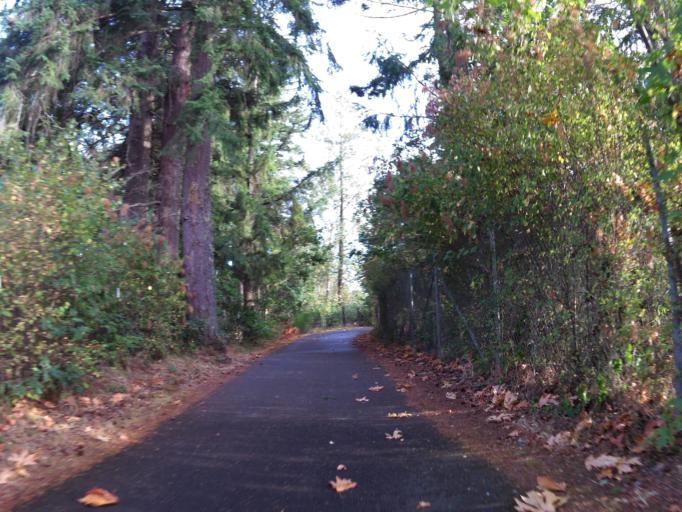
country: US
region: Washington
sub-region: Thurston County
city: Tenino
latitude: 46.9136
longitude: -122.7971
